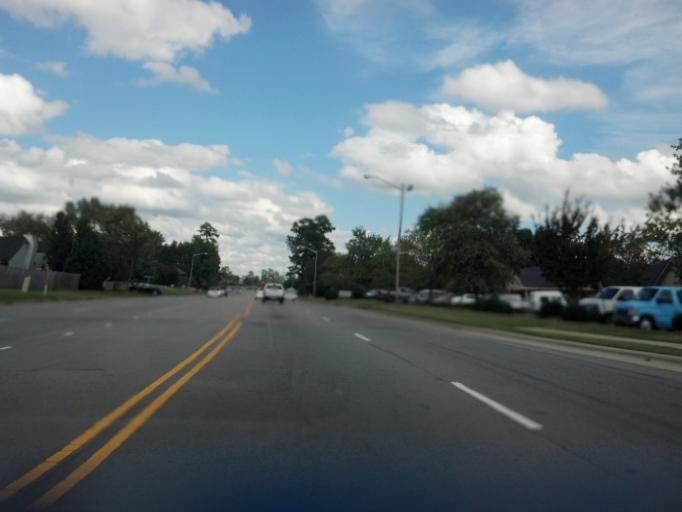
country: US
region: North Carolina
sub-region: Pitt County
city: Windsor
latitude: 35.5602
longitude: -77.3643
